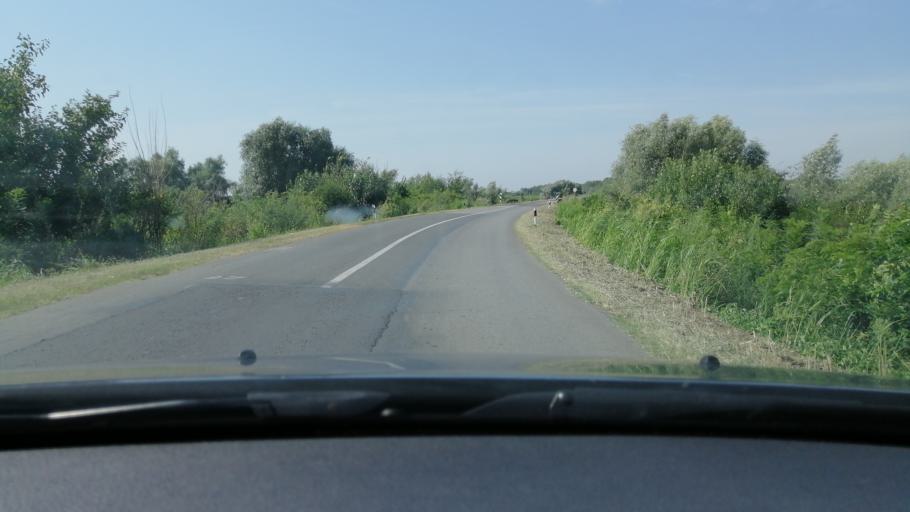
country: RS
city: Tomasevac
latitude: 45.2580
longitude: 20.6160
